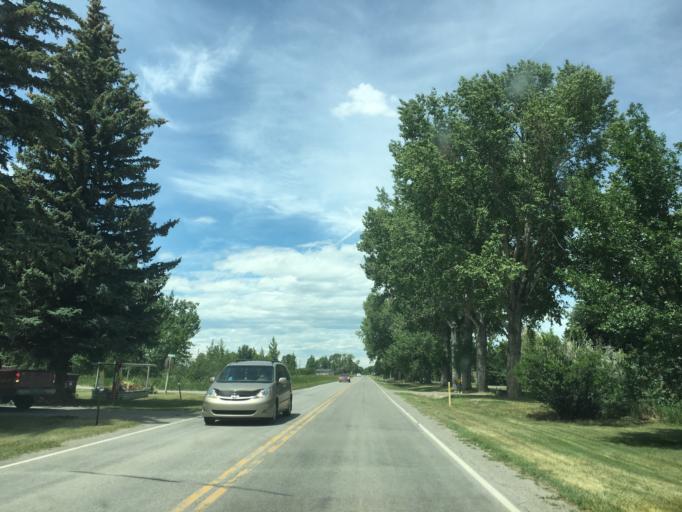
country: US
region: Montana
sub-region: Teton County
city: Choteau
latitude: 47.8240
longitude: -112.1925
